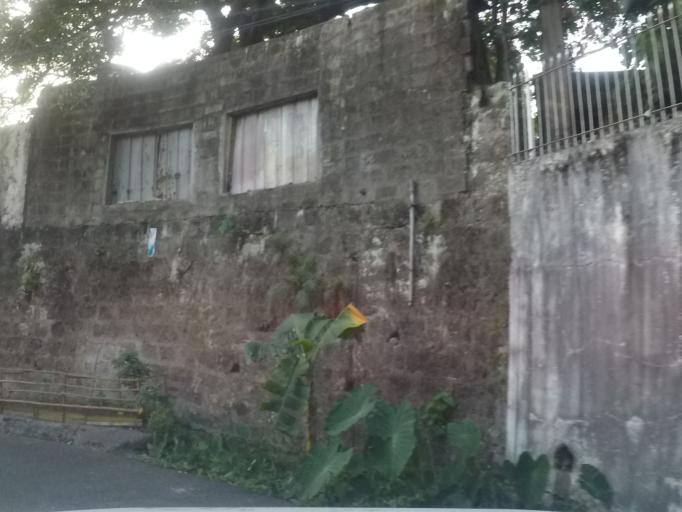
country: PH
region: Metro Manila
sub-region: San Juan
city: San Juan
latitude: 14.6032
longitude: 121.0284
